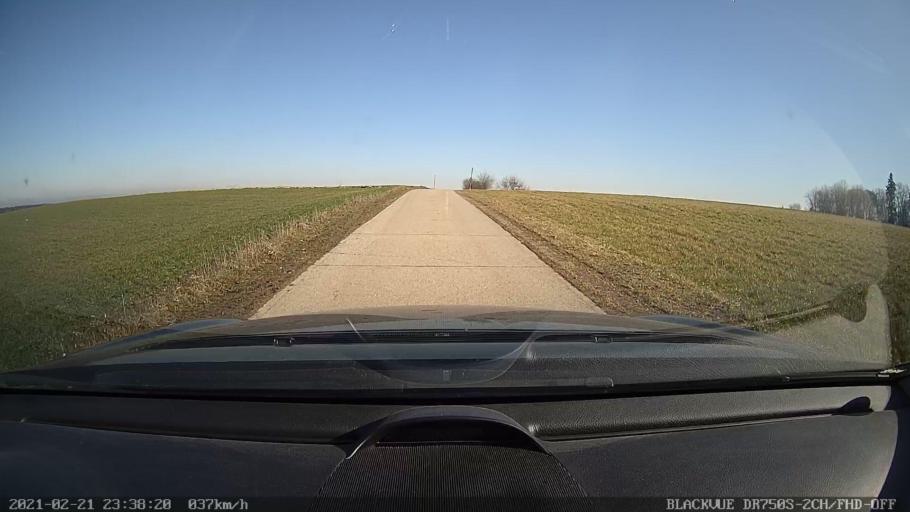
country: DE
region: Bavaria
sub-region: Upper Bavaria
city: Griesstatt
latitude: 47.9941
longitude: 12.2057
